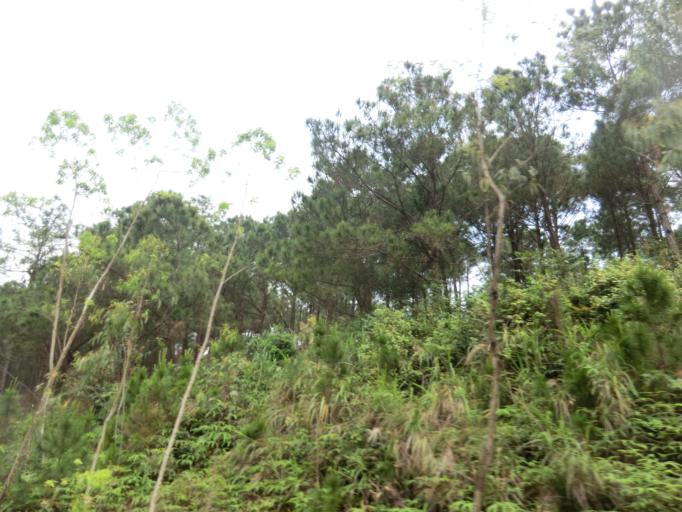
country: VN
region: Quang Binh
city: Ba Don
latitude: 17.6869
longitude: 106.4277
